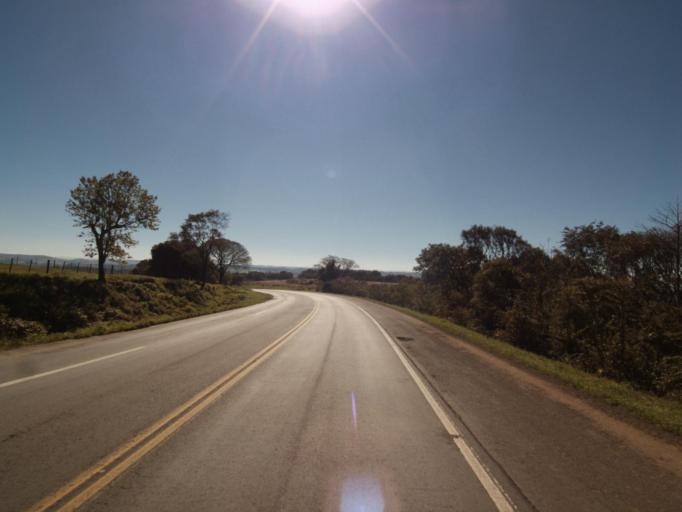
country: BR
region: Santa Catarina
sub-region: Sao Lourenco Do Oeste
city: Sao Lourenco dOeste
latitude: -26.8262
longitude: -53.1806
